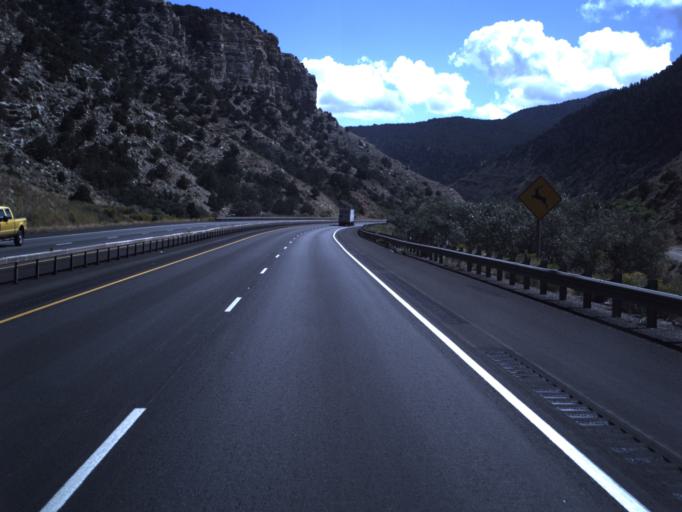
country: US
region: Utah
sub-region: Sevier County
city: Salina
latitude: 38.9011
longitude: -111.6668
